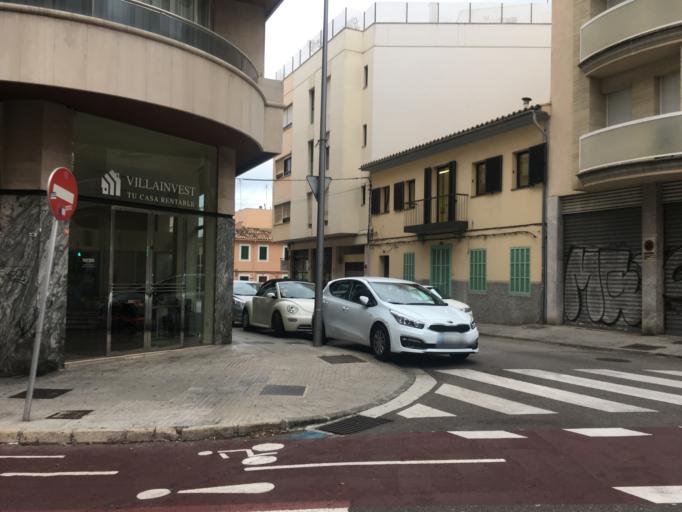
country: ES
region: Balearic Islands
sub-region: Illes Balears
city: Palma
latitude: 39.5736
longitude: 2.6396
